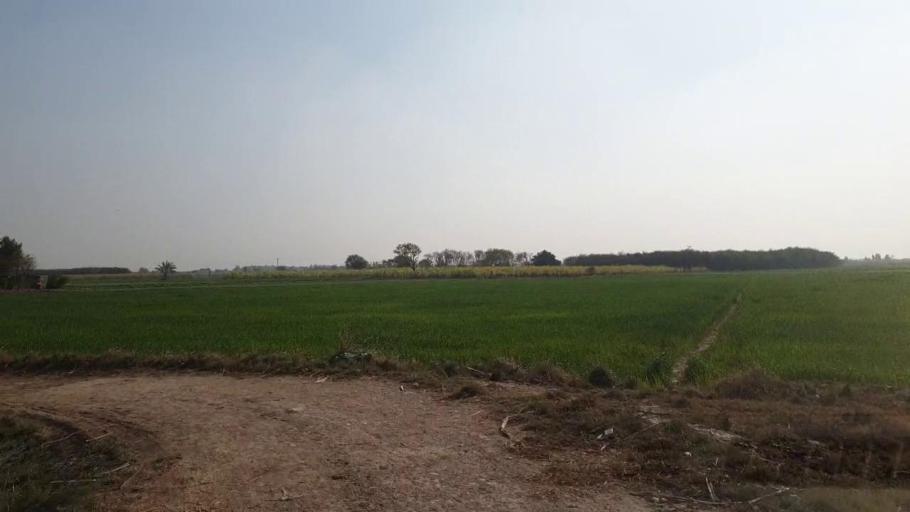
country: PK
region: Sindh
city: Tando Adam
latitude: 25.6603
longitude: 68.5695
